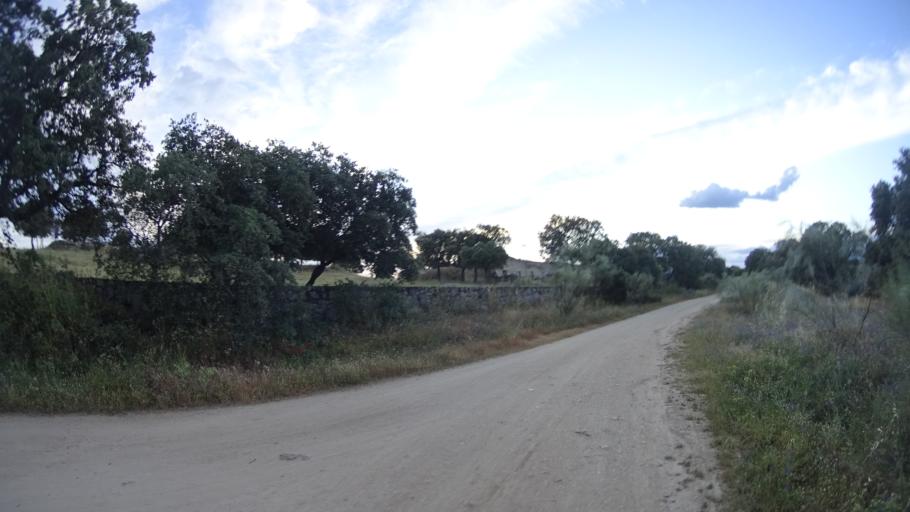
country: ES
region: Madrid
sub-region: Provincia de Madrid
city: Colmenarejo
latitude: 40.5351
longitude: -4.0071
